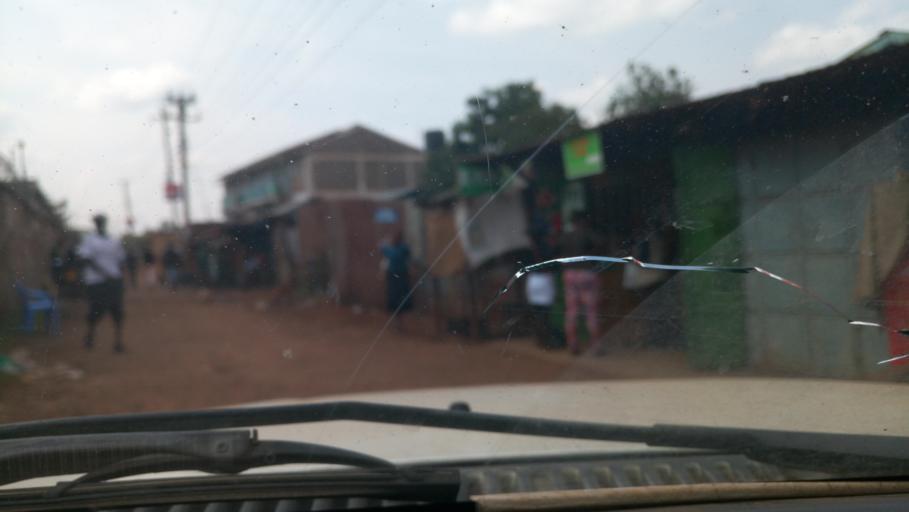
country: KE
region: Kiambu
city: Kikuyu
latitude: -1.2810
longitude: 36.6922
